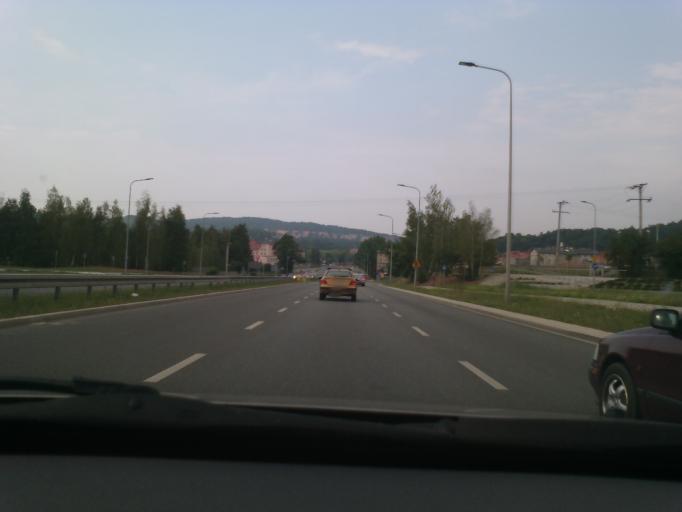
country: PL
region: Lower Silesian Voivodeship
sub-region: Powiat walbrzyski
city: Walbrzych
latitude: 50.7655
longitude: 16.2727
